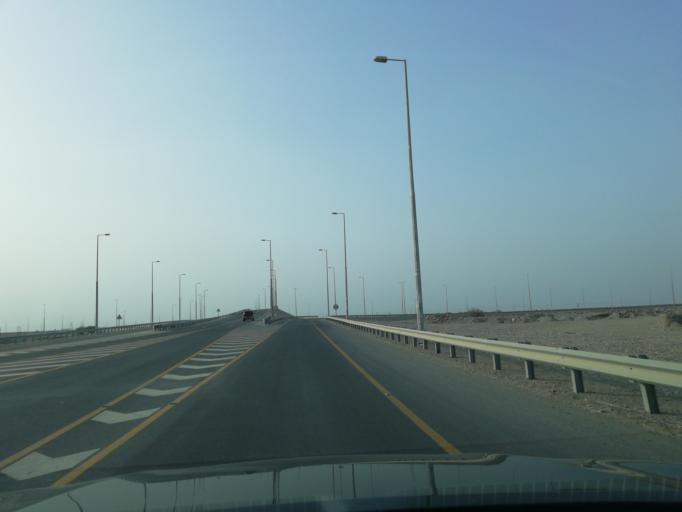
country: OM
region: Al Batinah
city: Barka'
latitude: 23.6157
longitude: 57.9092
